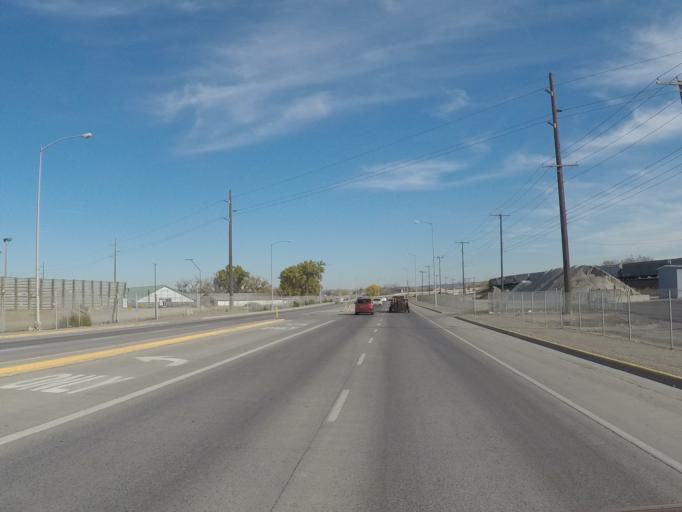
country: US
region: Montana
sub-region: Yellowstone County
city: Billings
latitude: 45.7954
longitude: -108.4769
